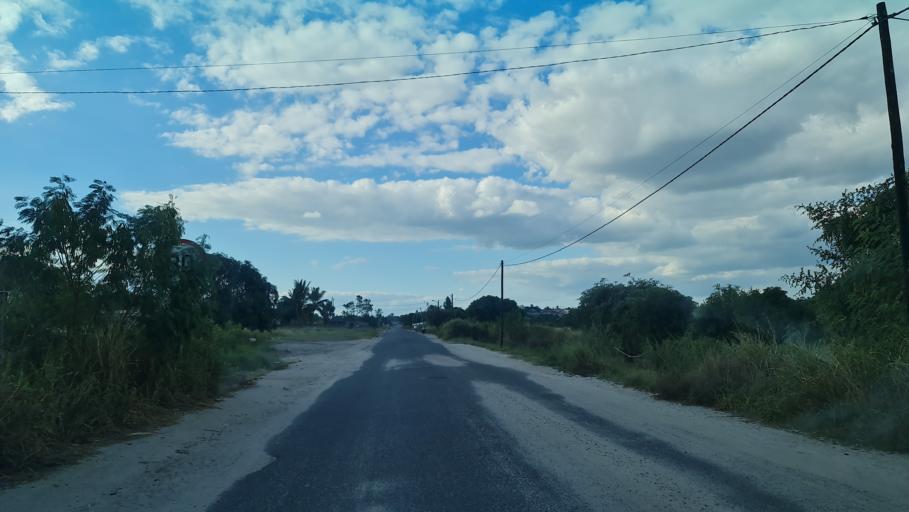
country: MZ
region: Manica
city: Chimoio
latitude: -19.2177
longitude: 33.9224
